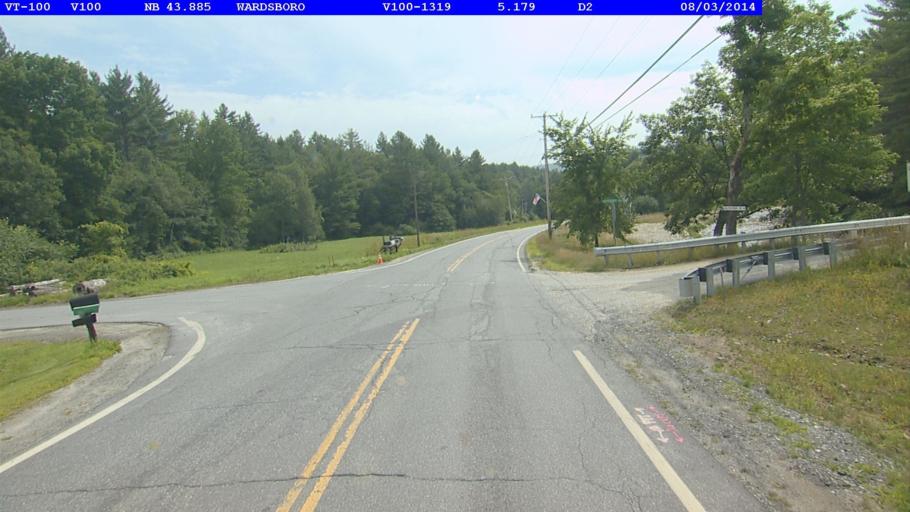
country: US
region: Vermont
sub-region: Windham County
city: Dover
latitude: 43.0347
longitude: -72.8106
